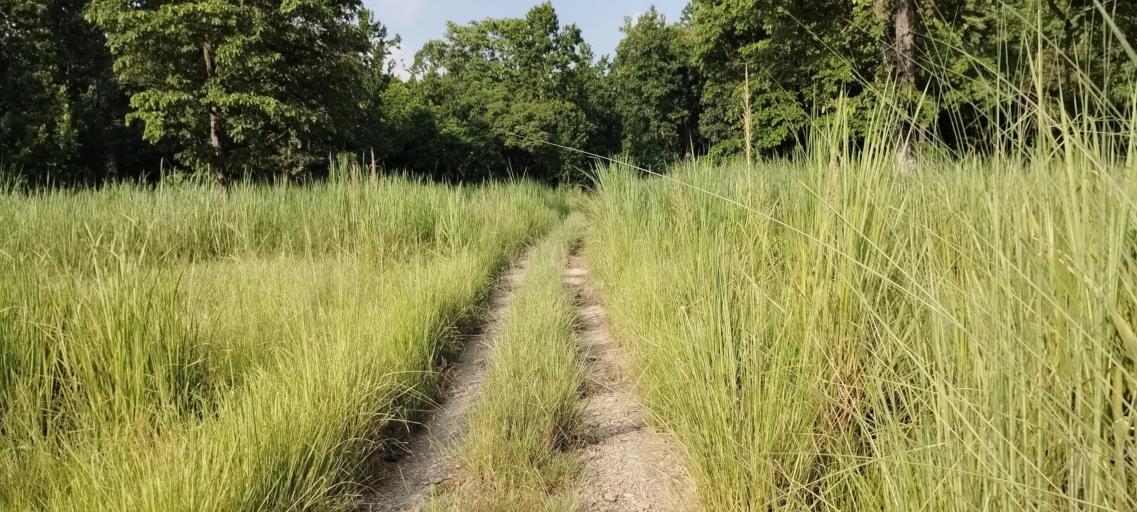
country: NP
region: Far Western
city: Tikapur
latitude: 28.5222
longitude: 81.2858
